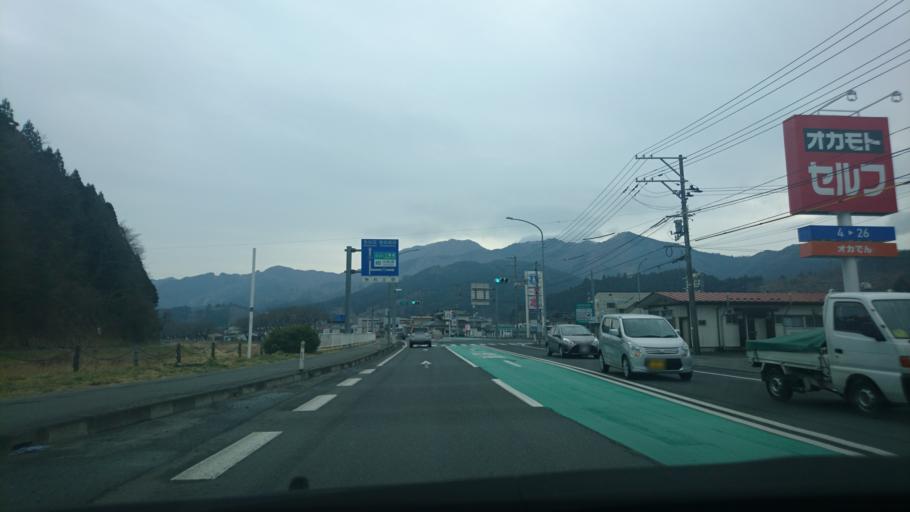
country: JP
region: Iwate
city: Ofunato
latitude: 39.0995
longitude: 141.7082
